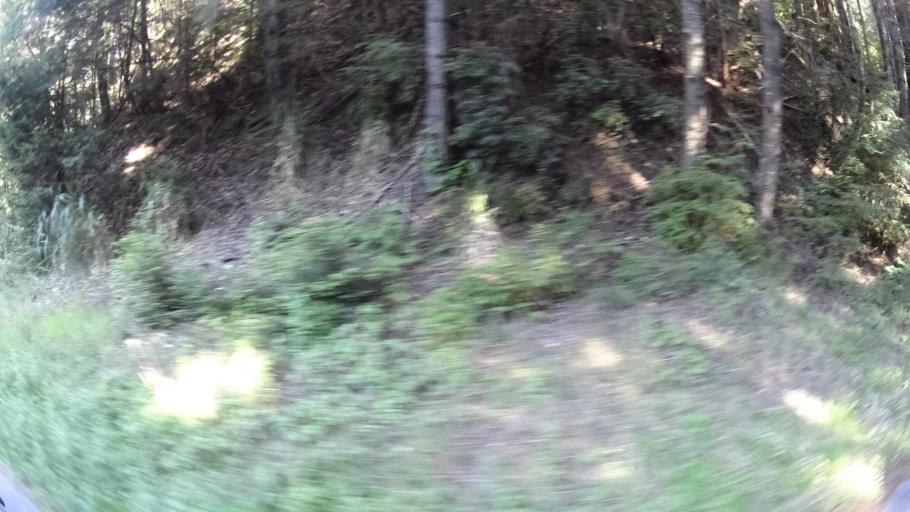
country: US
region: California
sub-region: Humboldt County
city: Rio Dell
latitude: 40.4605
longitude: -123.9986
